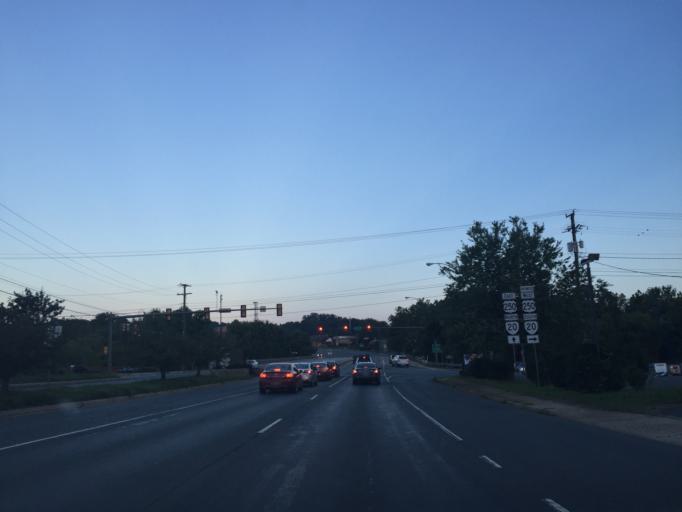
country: US
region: Virginia
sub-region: City of Charlottesville
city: Charlottesville
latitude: 38.0353
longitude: -78.4603
